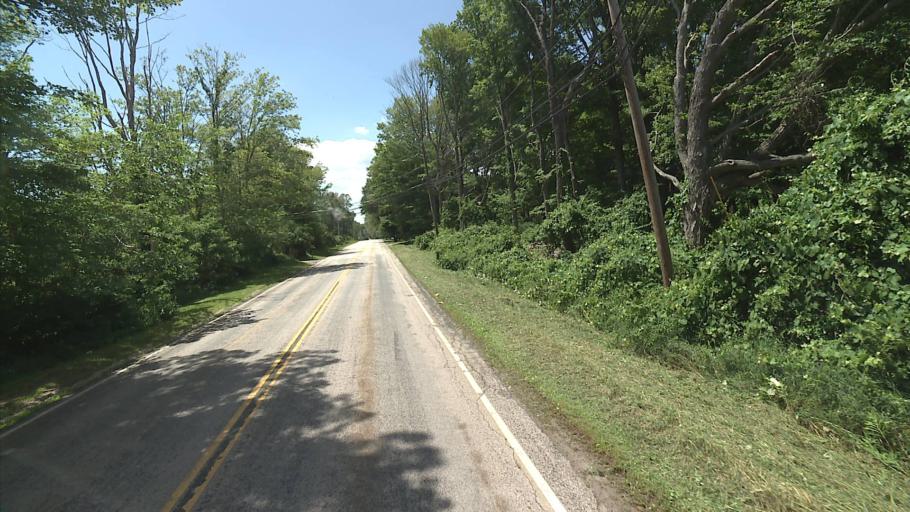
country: US
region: Connecticut
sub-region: Middlesex County
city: Moodus
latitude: 41.4711
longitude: -72.3944
